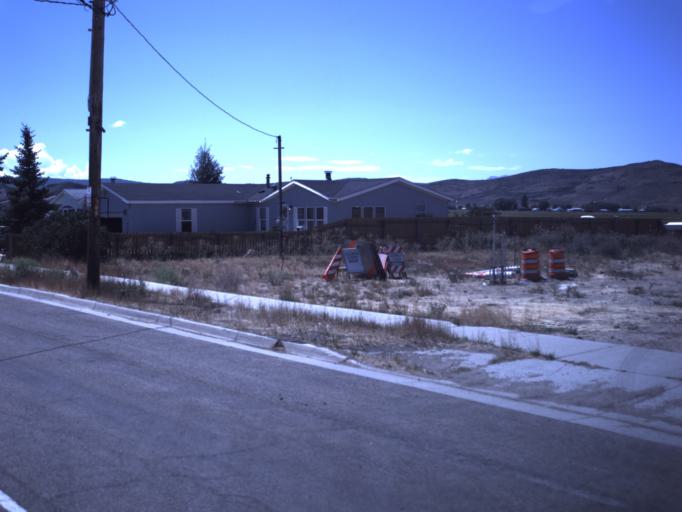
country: US
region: Utah
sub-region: Summit County
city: Kamas
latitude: 40.6357
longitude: -111.2808
